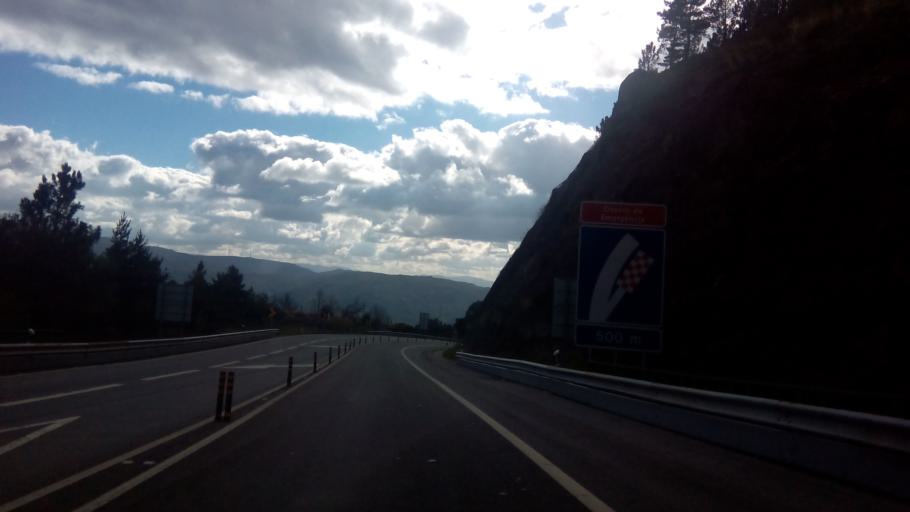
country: PT
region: Porto
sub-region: Baiao
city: Valadares
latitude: 41.2675
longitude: -7.9442
